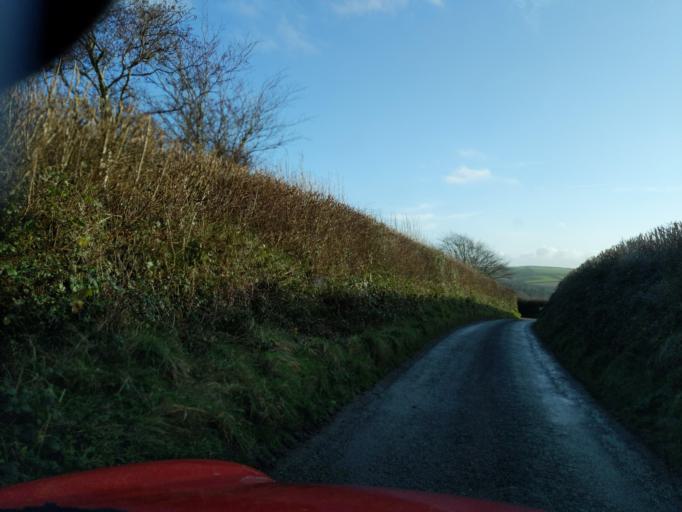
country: GB
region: England
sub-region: Cornwall
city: Fowey
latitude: 50.3521
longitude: -4.6064
